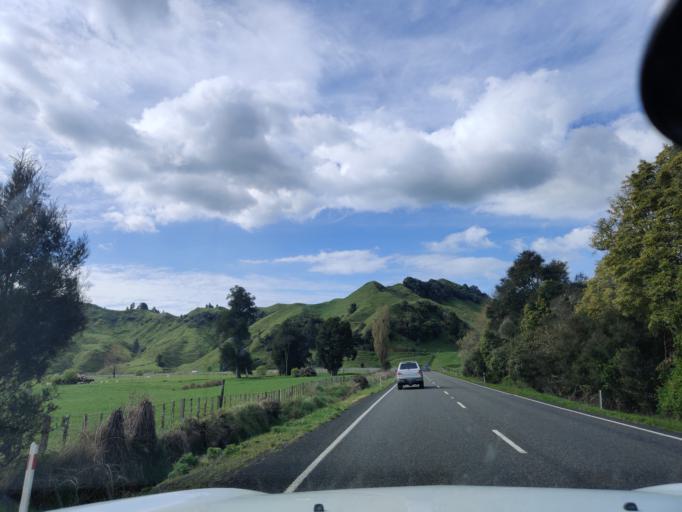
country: NZ
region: Waikato
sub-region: Otorohanga District
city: Otorohanga
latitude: -38.5549
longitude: 175.1951
